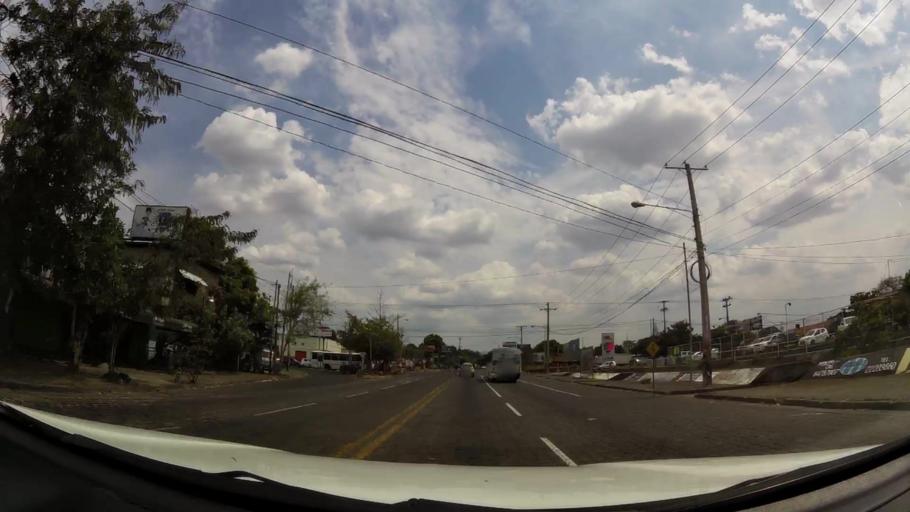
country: NI
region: Managua
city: Managua
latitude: 12.1467
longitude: -86.2412
